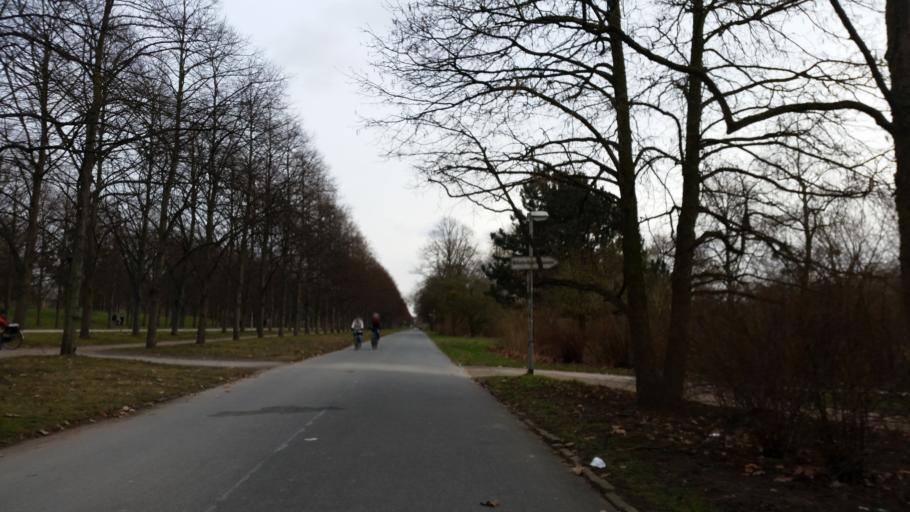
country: DE
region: Lower Saxony
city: Hannover
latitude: 52.3847
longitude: 9.7111
